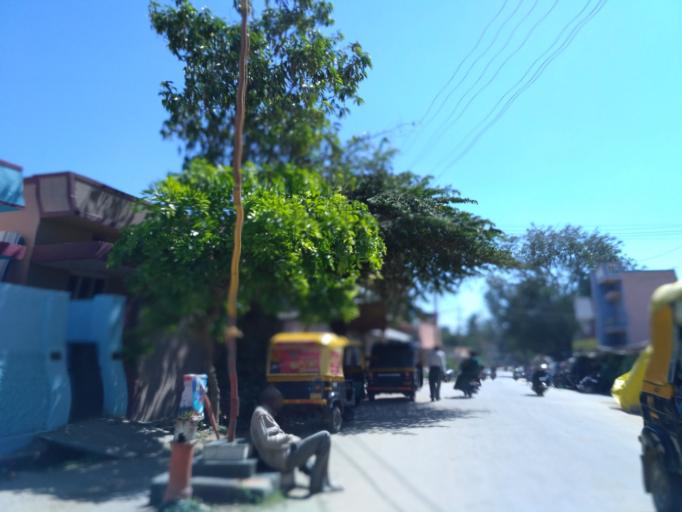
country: IN
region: Karnataka
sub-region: Hassan
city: Hassan
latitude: 13.0173
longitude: 76.0941
